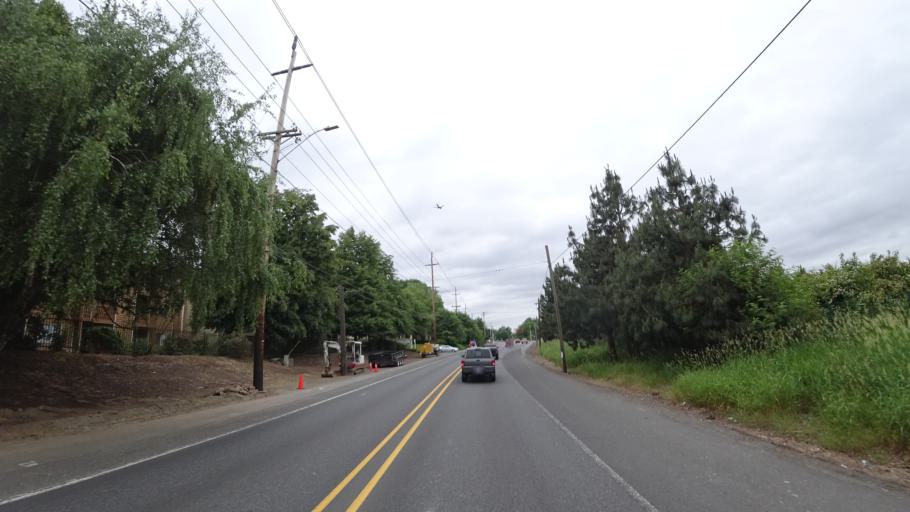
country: US
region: Oregon
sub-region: Multnomah County
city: Fairview
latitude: 45.5499
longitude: -122.4980
